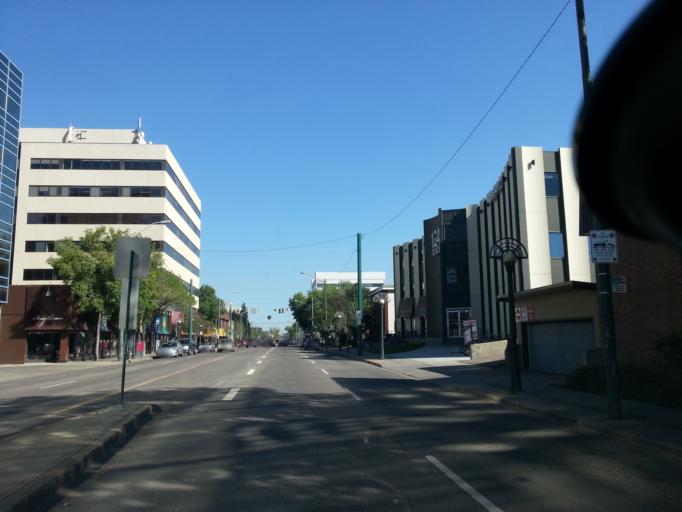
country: CA
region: Alberta
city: Edmonton
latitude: 53.5436
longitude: -113.5359
